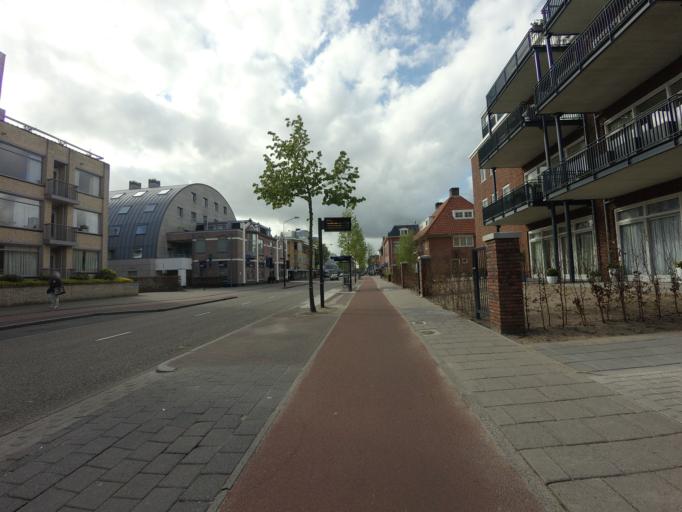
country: NL
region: Utrecht
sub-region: Gemeente Zeist
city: Zeist
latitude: 52.0841
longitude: 5.2439
